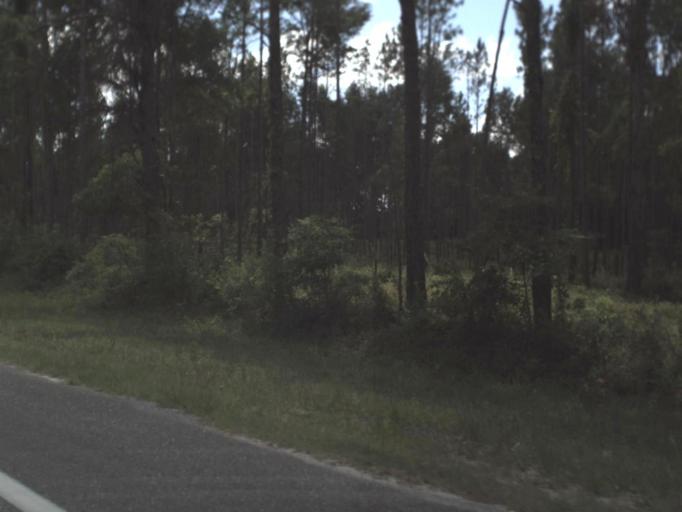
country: US
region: Florida
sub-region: Suwannee County
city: Wellborn
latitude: 30.3202
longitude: -82.7988
